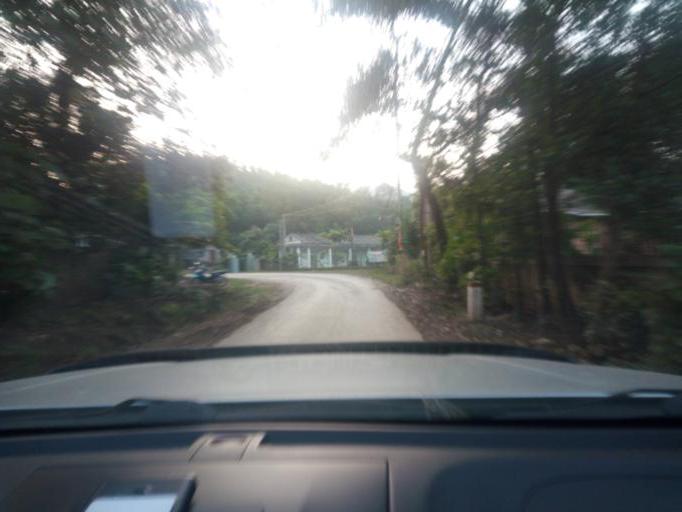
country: VN
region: Yen Bai
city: Co Phuc
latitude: 21.8614
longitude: 104.6237
